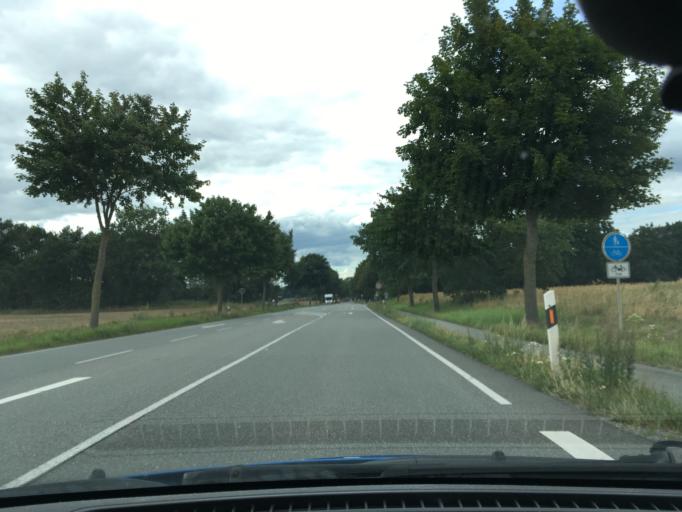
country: DE
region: Lower Saxony
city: Neu Wulmstorf
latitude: 53.4408
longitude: 9.7639
